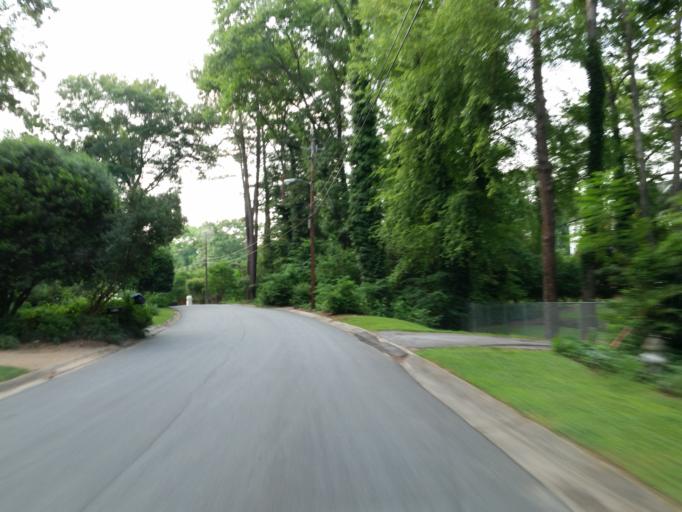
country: US
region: Georgia
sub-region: Cobb County
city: Vinings
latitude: 33.8616
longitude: -84.4574
